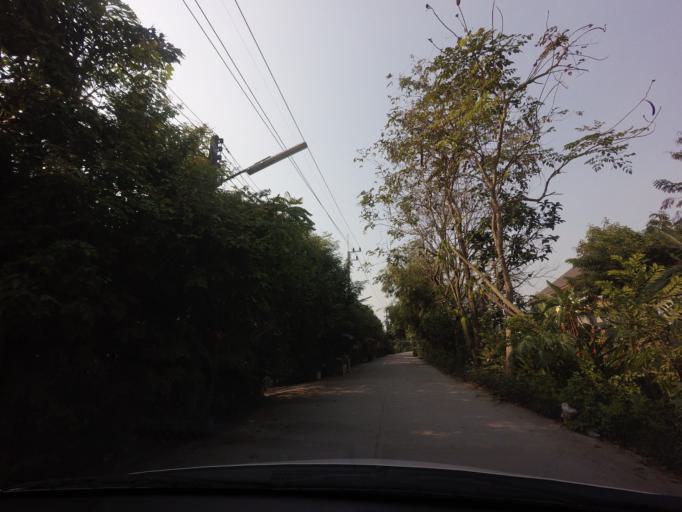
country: TH
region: Samut Sakhon
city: Krathum Baen
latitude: 13.6888
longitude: 100.2519
